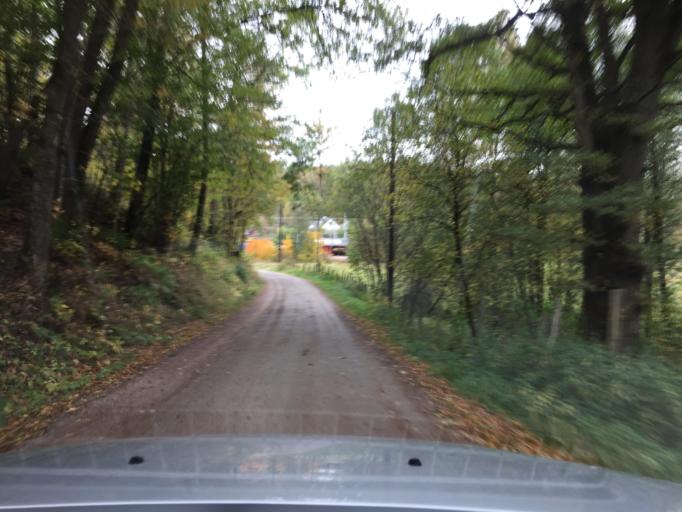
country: SE
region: Skane
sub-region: Hassleholms Kommun
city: Tormestorp
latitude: 56.0702
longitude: 13.7382
